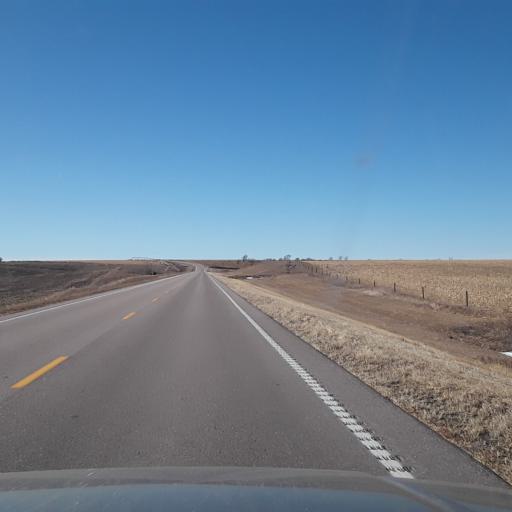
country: US
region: Nebraska
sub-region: Frontier County
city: Stockville
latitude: 40.7057
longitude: -100.2326
